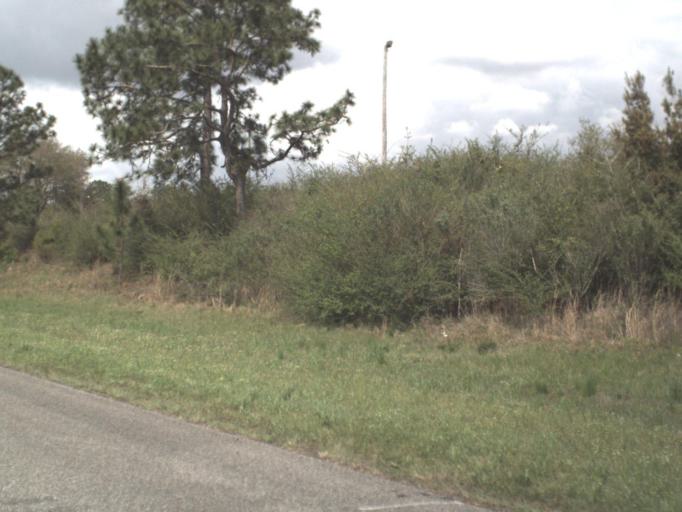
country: US
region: Florida
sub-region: Okaloosa County
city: Crestview
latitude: 30.6860
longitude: -86.7895
